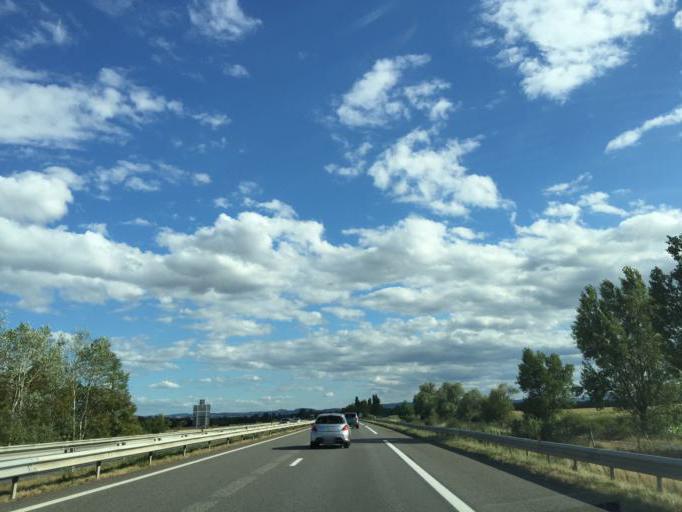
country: FR
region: Rhone-Alpes
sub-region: Departement de la Loire
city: Cuzieu
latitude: 45.5904
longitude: 4.2112
